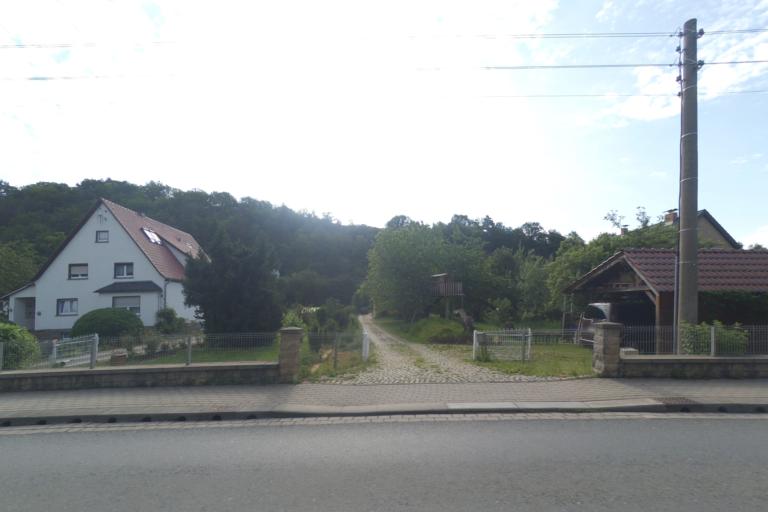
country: DE
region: Thuringia
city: Kaulsdorf
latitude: 50.6246
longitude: 11.4295
